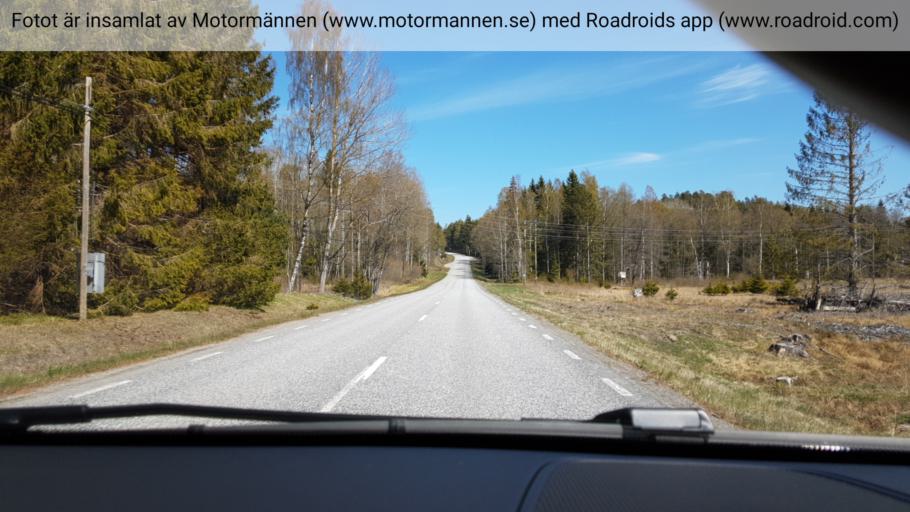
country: SE
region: Stockholm
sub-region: Haninge Kommun
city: Jordbro
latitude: 58.9877
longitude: 18.0961
